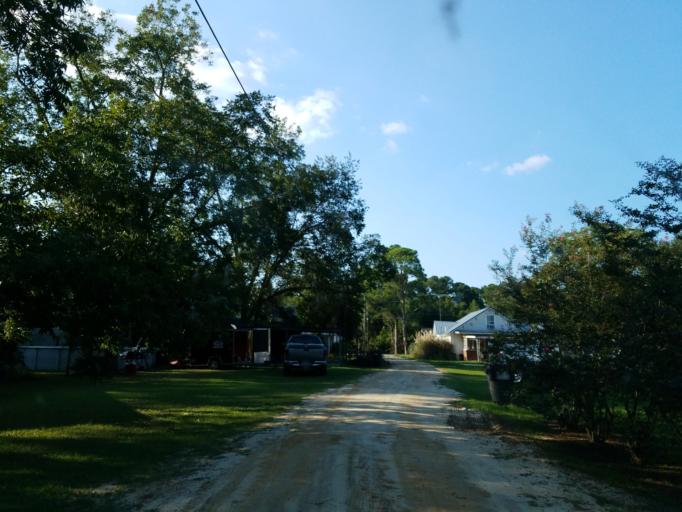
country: US
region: Georgia
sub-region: Cook County
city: Sparks
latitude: 31.2705
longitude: -83.4671
